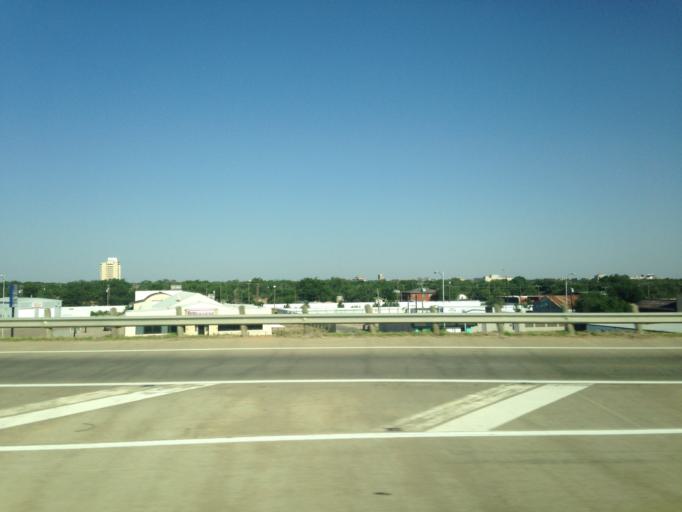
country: US
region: Texas
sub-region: Lubbock County
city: Lubbock
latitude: 33.5706
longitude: -101.8445
